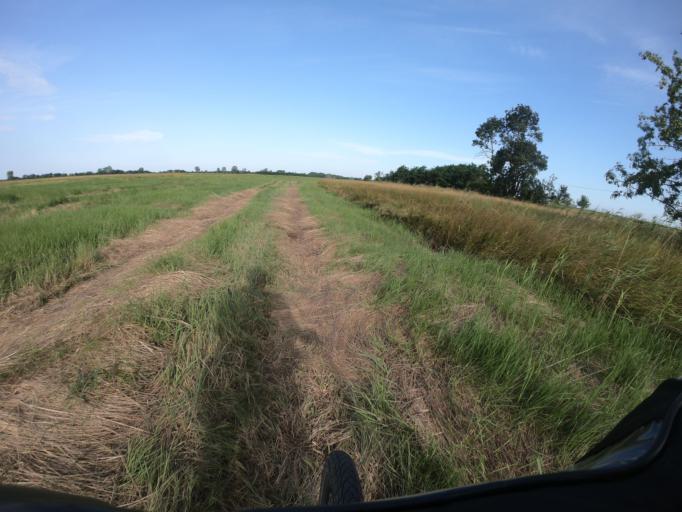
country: HU
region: Hajdu-Bihar
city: Tiszacsege
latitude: 47.6134
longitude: 21.0249
